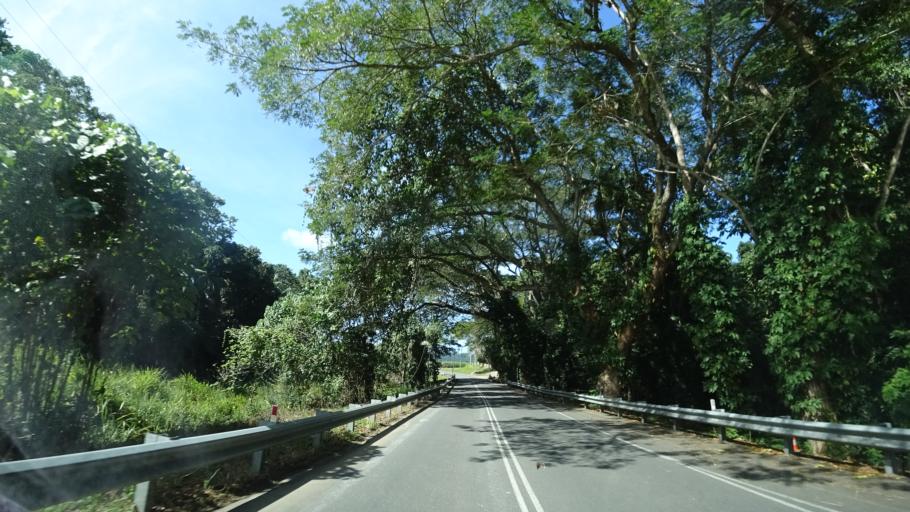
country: AU
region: Queensland
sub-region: Cairns
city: Port Douglas
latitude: -16.4669
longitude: 145.3638
